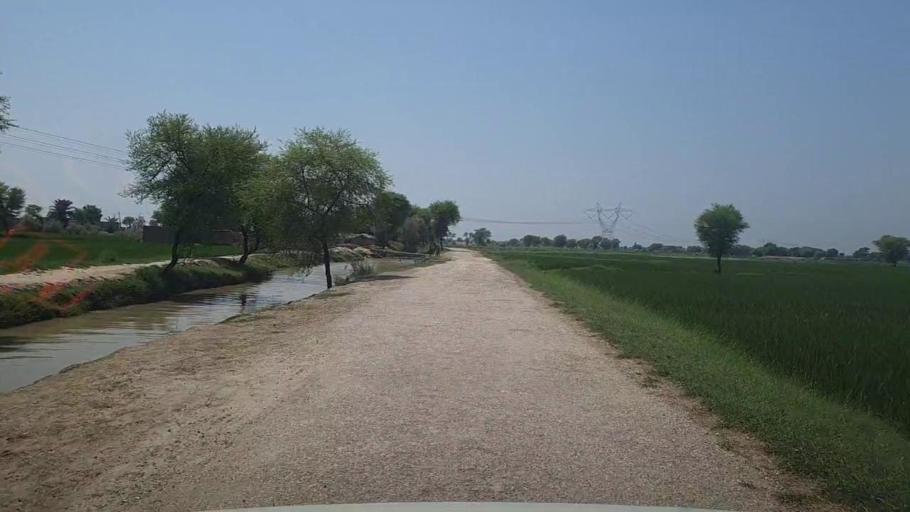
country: PK
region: Sindh
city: Kandhkot
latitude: 28.3259
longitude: 69.3842
